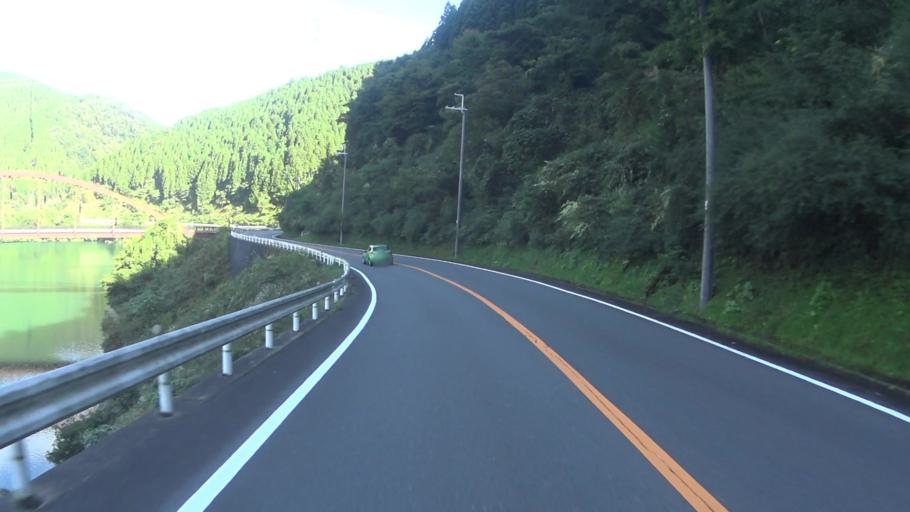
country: JP
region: Kyoto
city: Kameoka
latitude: 35.1311
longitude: 135.5558
